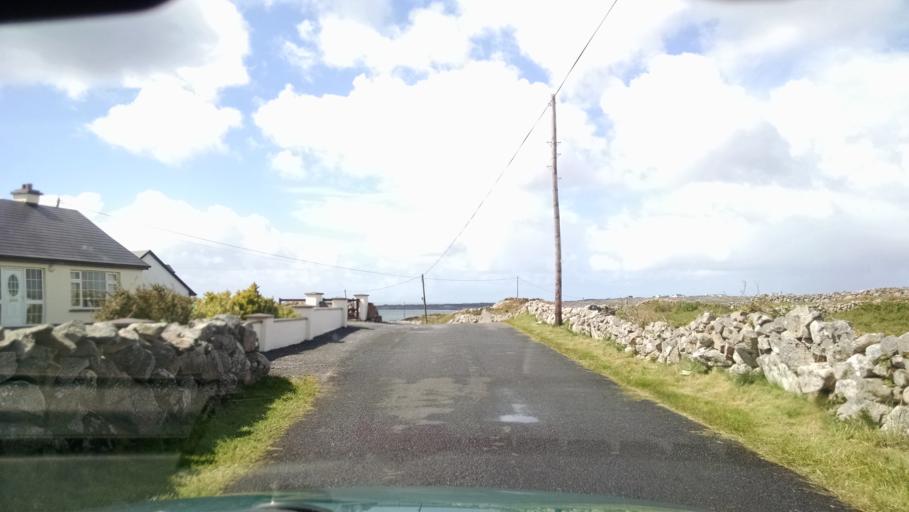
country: IE
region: Connaught
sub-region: County Galway
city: Oughterard
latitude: 53.2473
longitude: -9.6241
